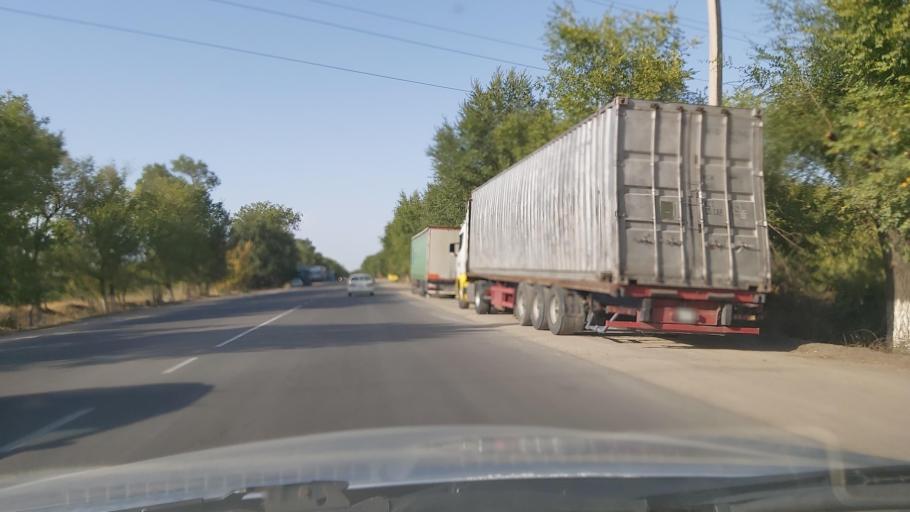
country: KZ
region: Almaty Oblysy
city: Energeticheskiy
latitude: 43.5184
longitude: 77.0470
